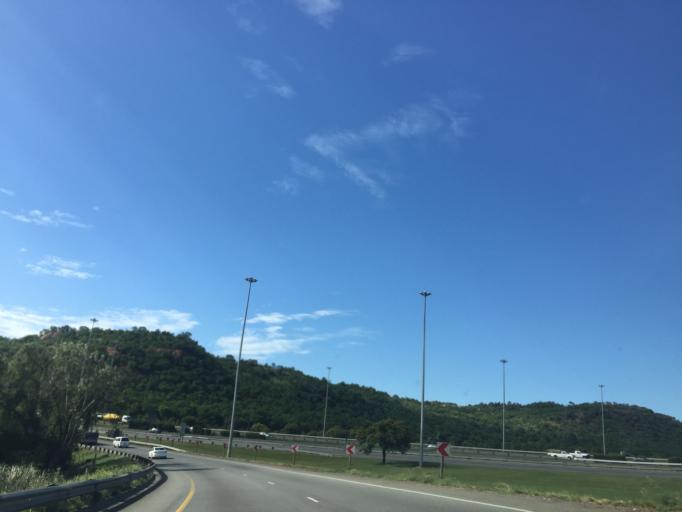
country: ZA
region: Gauteng
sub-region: City of Johannesburg Metropolitan Municipality
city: Johannesburg
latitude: -26.2655
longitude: 28.0972
